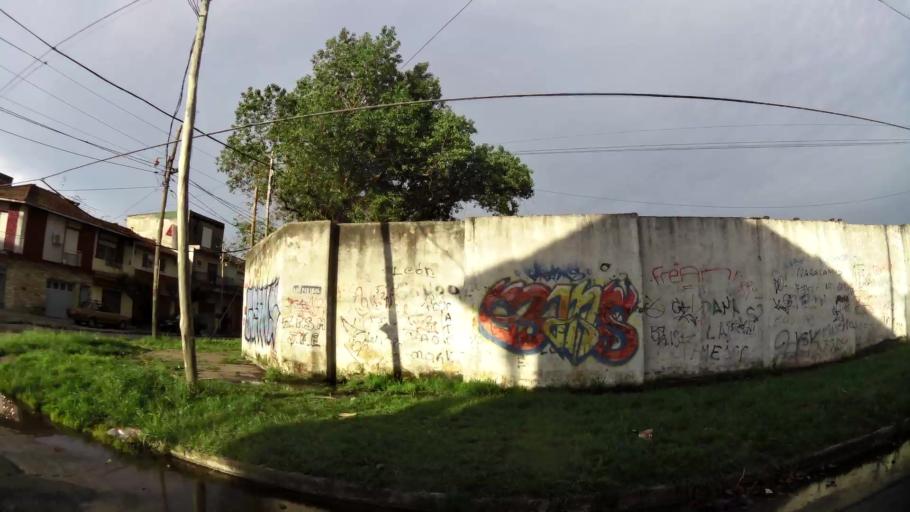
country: AR
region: Buenos Aires
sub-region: Partido de Lomas de Zamora
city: Lomas de Zamora
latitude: -34.7445
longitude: -58.3502
